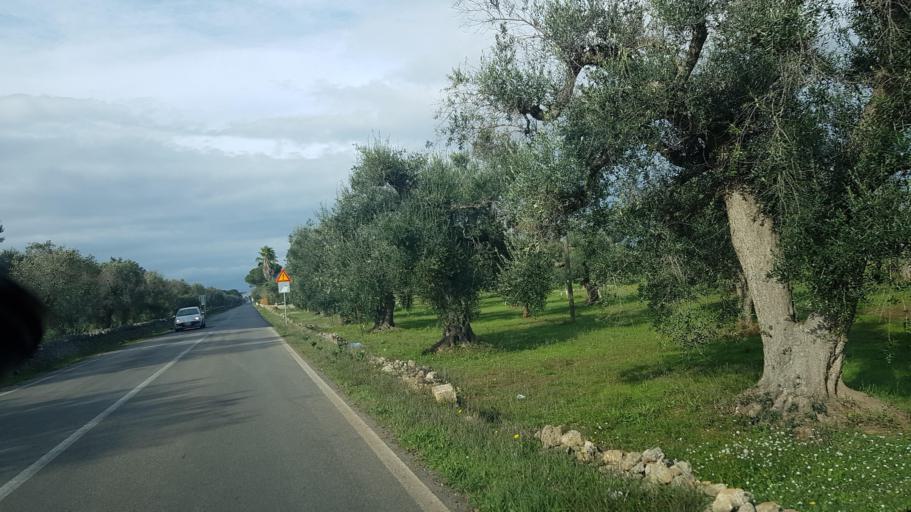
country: IT
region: Apulia
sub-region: Provincia di Brindisi
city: Oria
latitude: 40.4813
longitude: 17.6863
